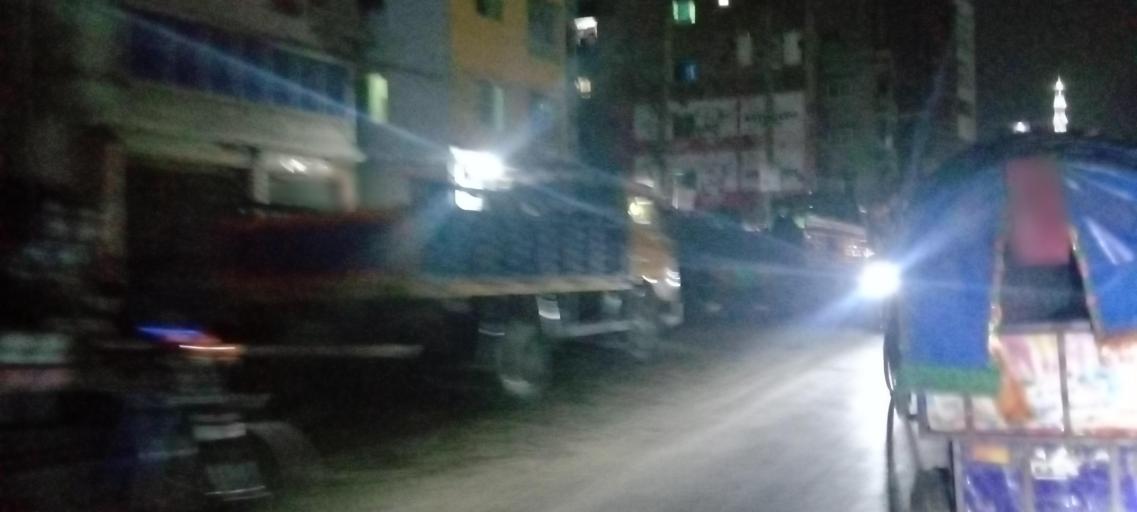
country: BD
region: Dhaka
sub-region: Dhaka
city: Dhaka
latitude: 23.7013
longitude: 90.3927
